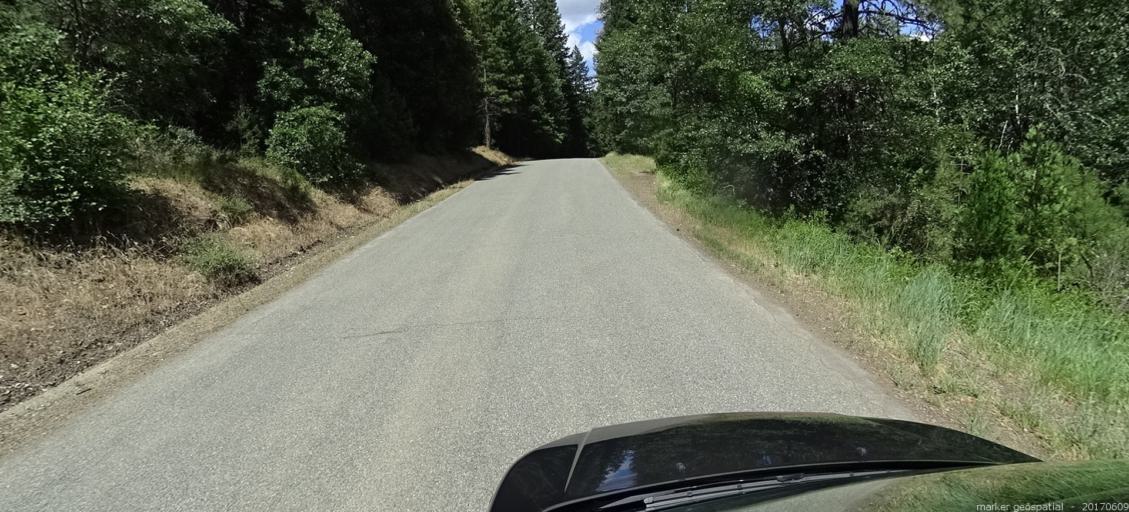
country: US
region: California
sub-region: Siskiyou County
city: Yreka
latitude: 41.4346
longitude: -122.9150
